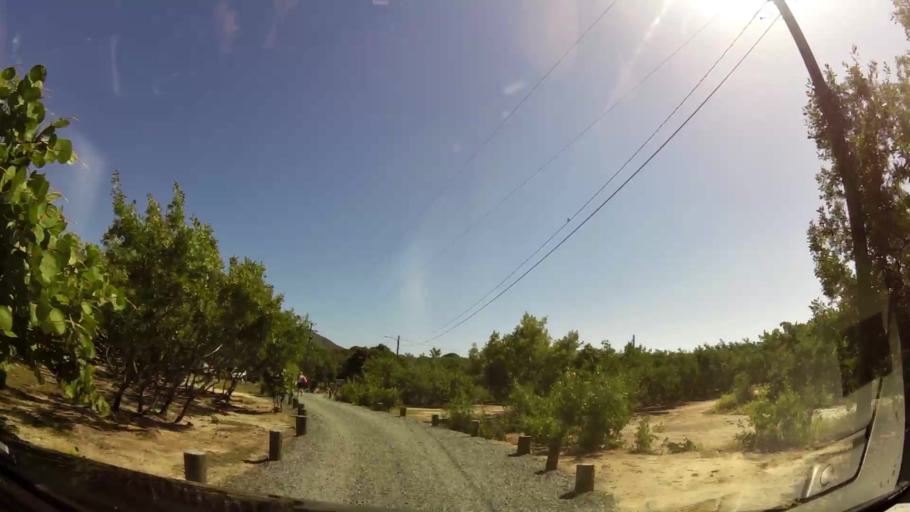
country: VG
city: Tortola
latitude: 18.4446
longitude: -64.5339
